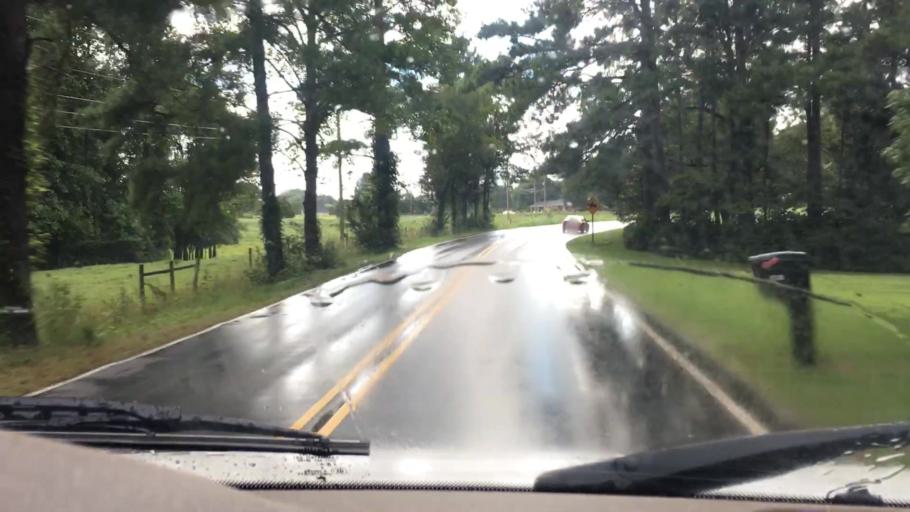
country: US
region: North Carolina
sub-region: Mecklenburg County
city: Huntersville
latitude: 35.4196
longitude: -80.9116
